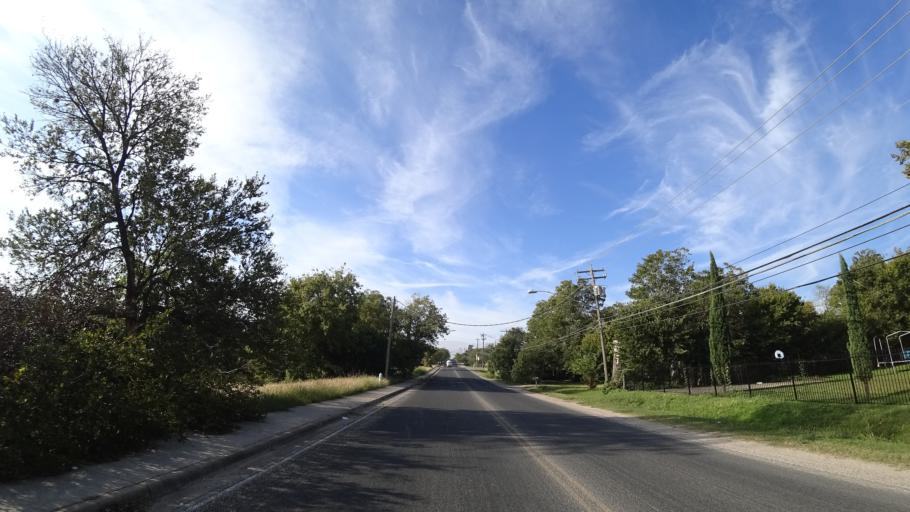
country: US
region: Texas
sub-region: Travis County
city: Austin
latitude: 30.1967
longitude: -97.7367
